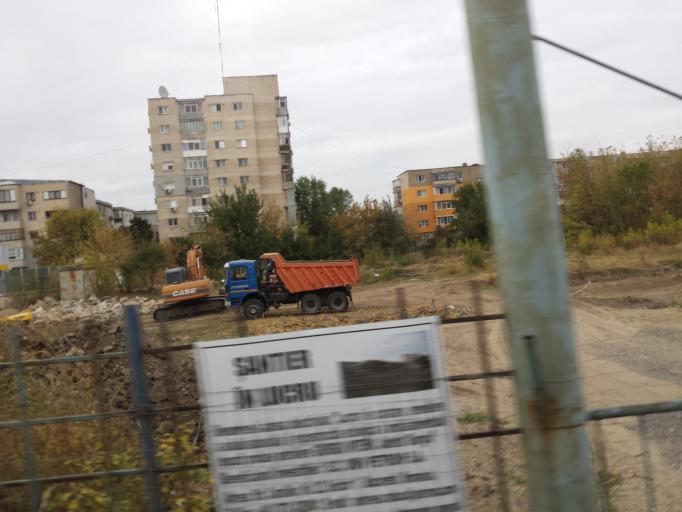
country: RO
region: Giurgiu
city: Giurgiu
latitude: 43.9052
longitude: 25.9718
